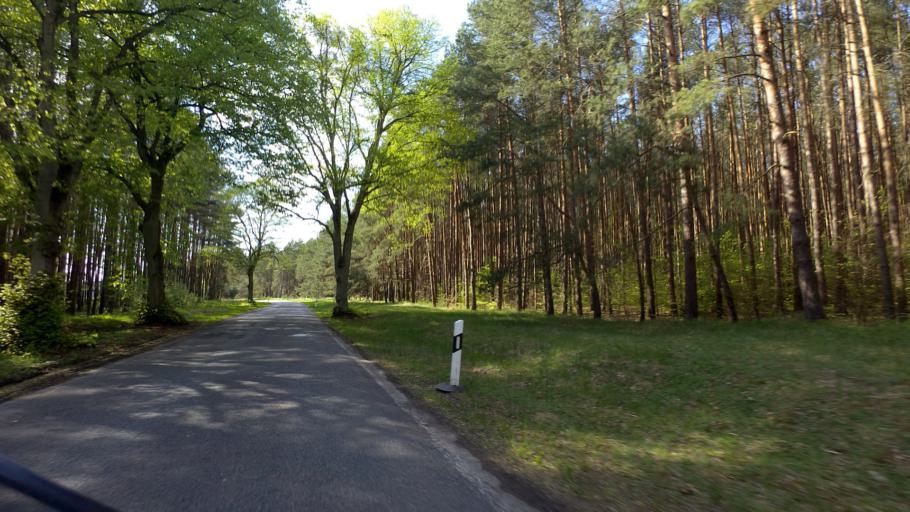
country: DE
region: Brandenburg
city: Templin
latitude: 53.0000
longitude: 13.4986
